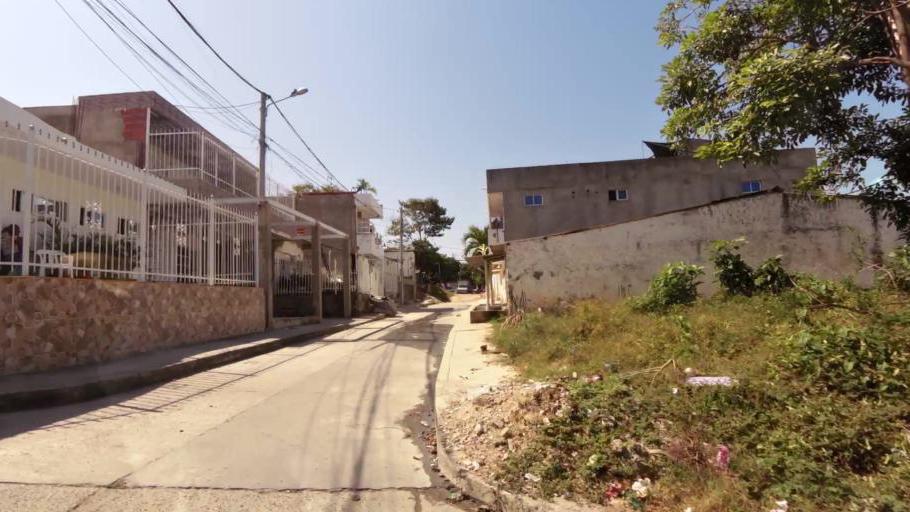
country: CO
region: Bolivar
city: Cartagena
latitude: 10.3909
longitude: -75.5125
